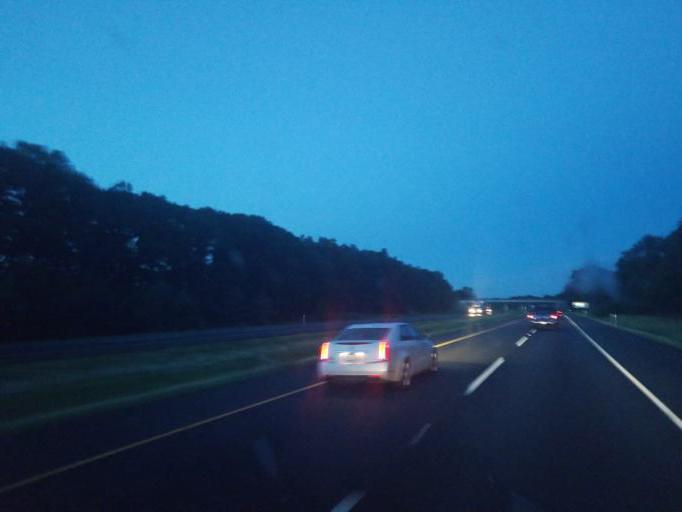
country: US
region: Indiana
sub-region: Saint Joseph County
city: Granger
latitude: 41.7311
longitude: -86.0548
